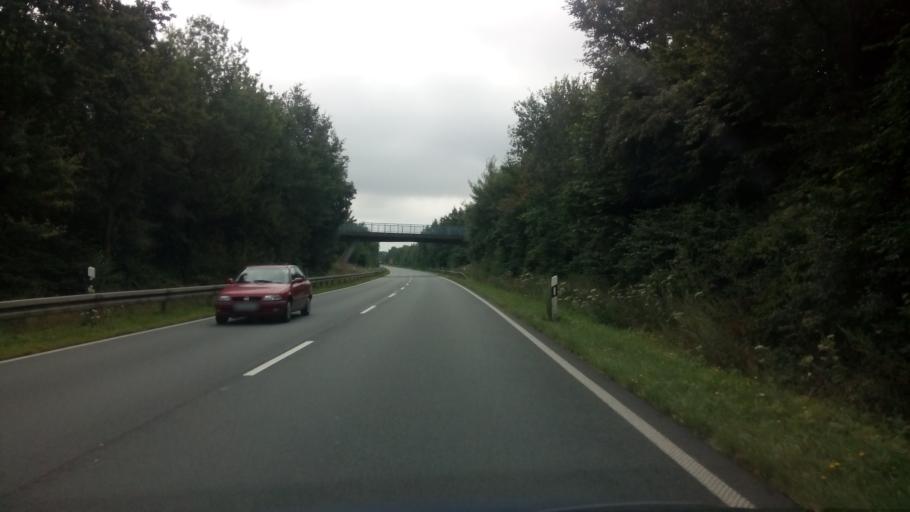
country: DE
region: Lower Saxony
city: Bassum
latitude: 52.8673
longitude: 8.7332
